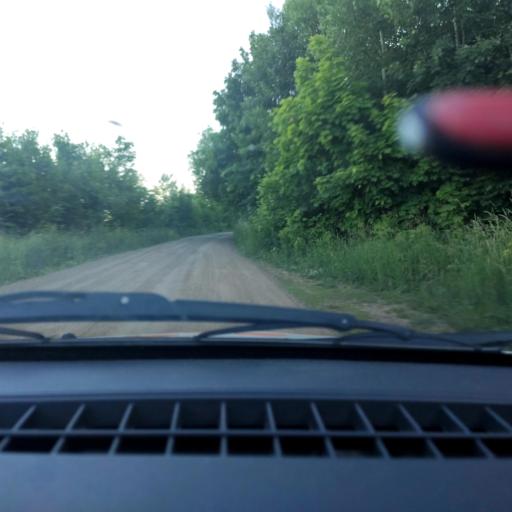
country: RU
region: Bashkortostan
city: Karmaskaly
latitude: 54.3747
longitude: 55.9109
